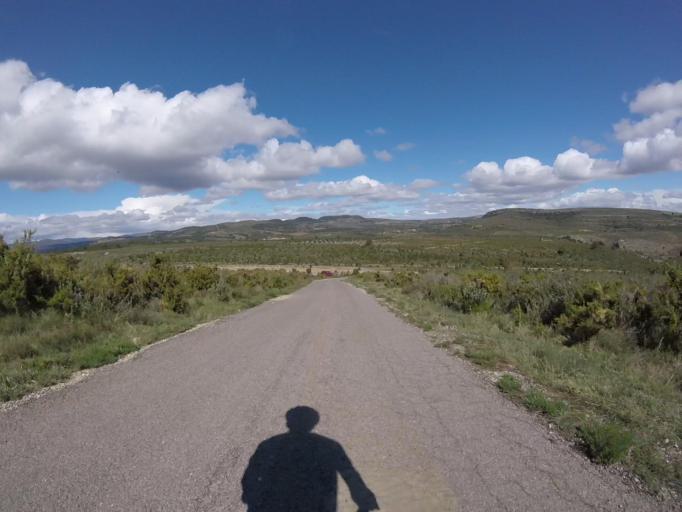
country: ES
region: Valencia
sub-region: Provincia de Castello
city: Culla
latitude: 40.3060
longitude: -0.1170
